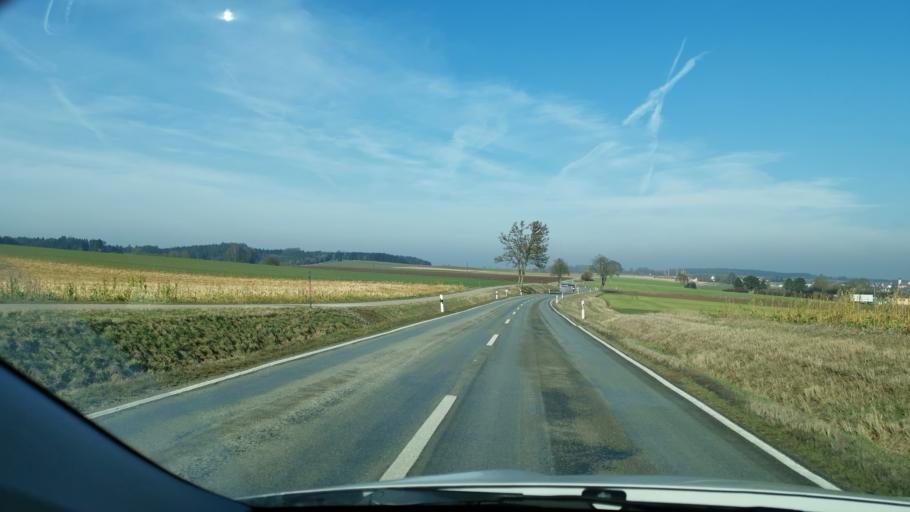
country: DE
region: Bavaria
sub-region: Swabia
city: Holzheim
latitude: 48.5951
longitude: 10.9541
